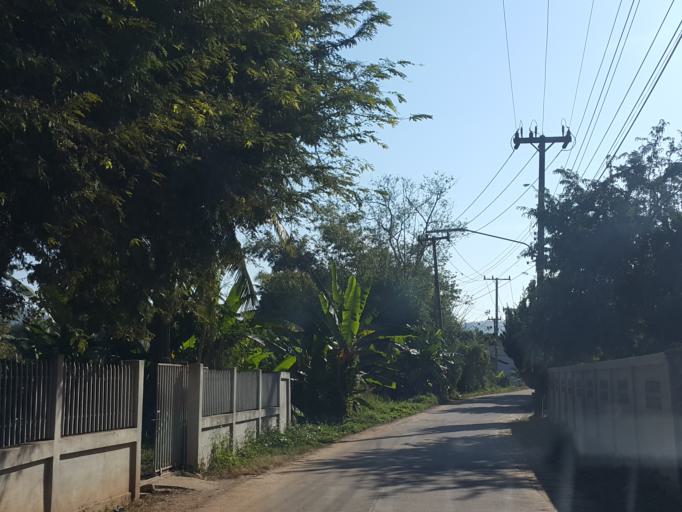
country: TH
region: Chiang Mai
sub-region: Amphoe Chiang Dao
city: Chiang Dao
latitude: 19.4674
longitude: 98.9567
